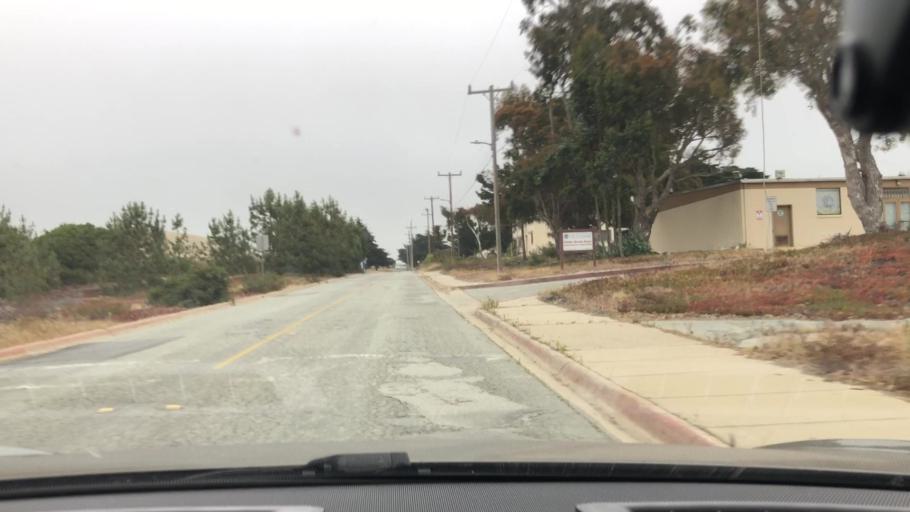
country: US
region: California
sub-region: Monterey County
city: Marina
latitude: 36.6463
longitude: -121.7954
